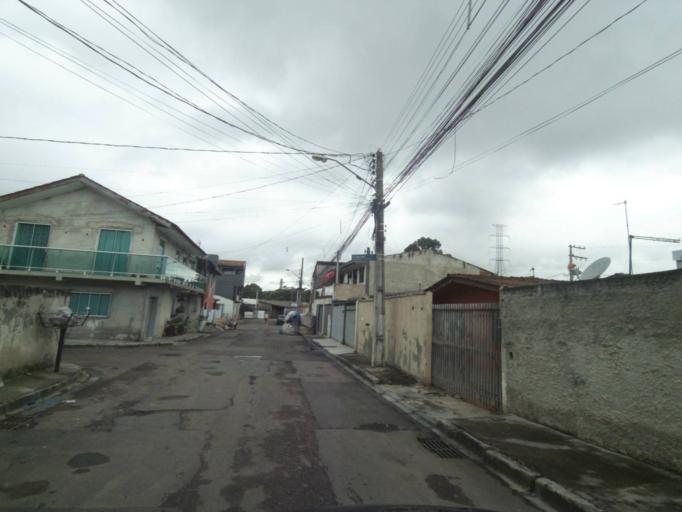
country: BR
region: Parana
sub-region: Curitiba
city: Curitiba
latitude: -25.4683
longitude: -49.3226
